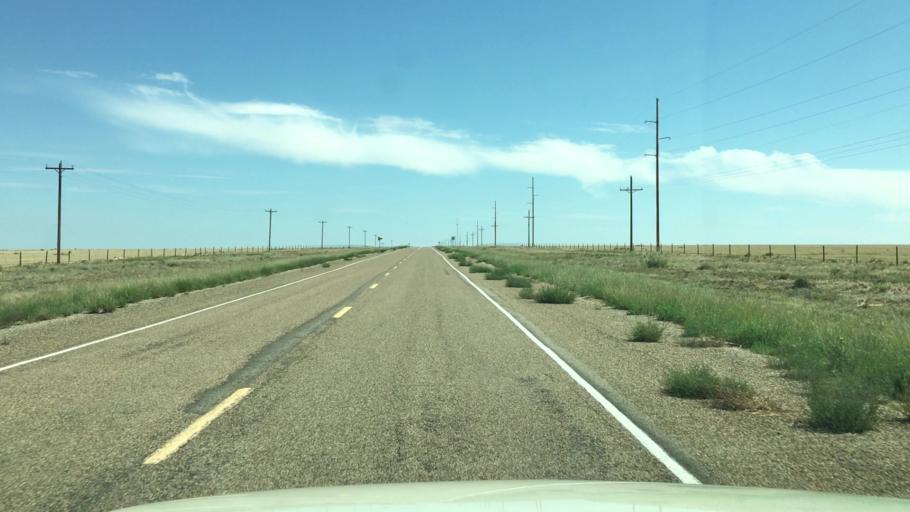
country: US
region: New Mexico
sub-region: Chaves County
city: Roswell
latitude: 33.9425
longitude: -104.5918
